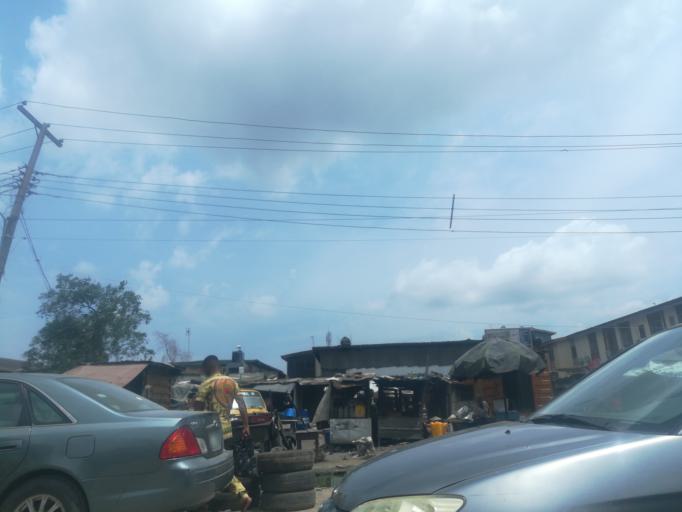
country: NG
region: Lagos
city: Somolu
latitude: 6.5576
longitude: 3.3904
